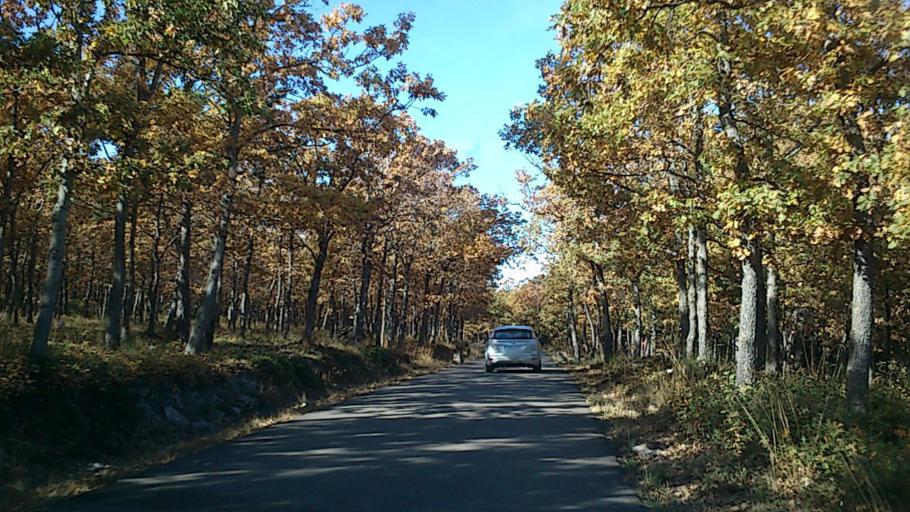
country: ES
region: Aragon
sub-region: Provincia de Zaragoza
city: Lituenigo
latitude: 41.8099
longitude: -1.8050
